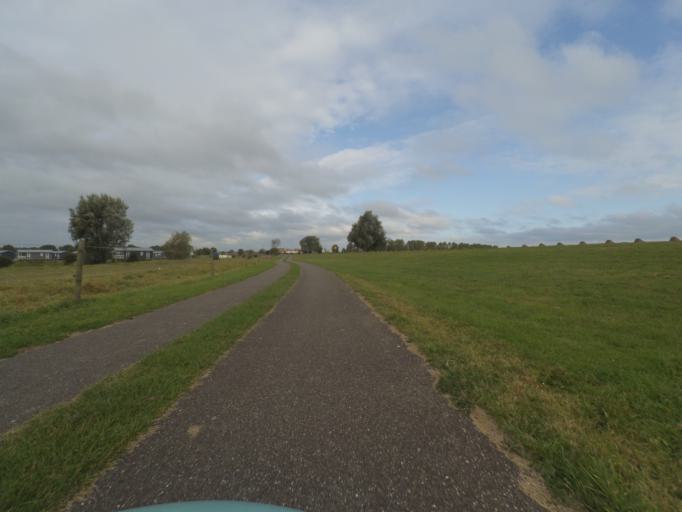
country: NL
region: Utrecht
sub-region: Gemeente Utrechtse Heuvelrug
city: Leersum
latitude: 51.9741
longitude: 5.4326
